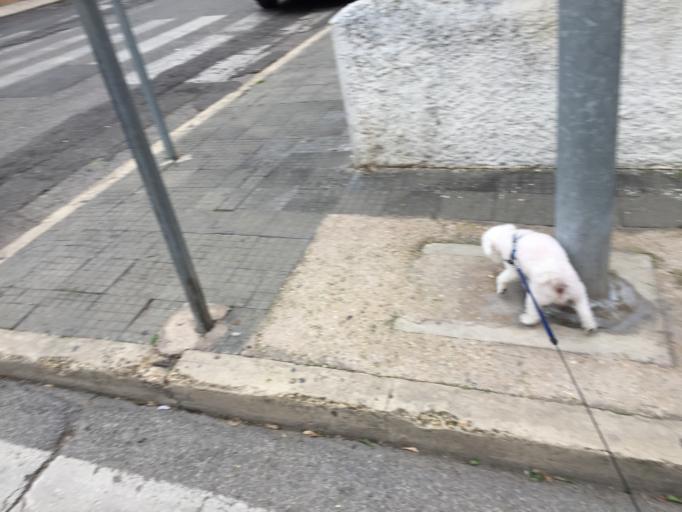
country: IT
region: Latium
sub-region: Citta metropolitana di Roma Capitale
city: Ladispoli
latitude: 41.9548
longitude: 12.0655
